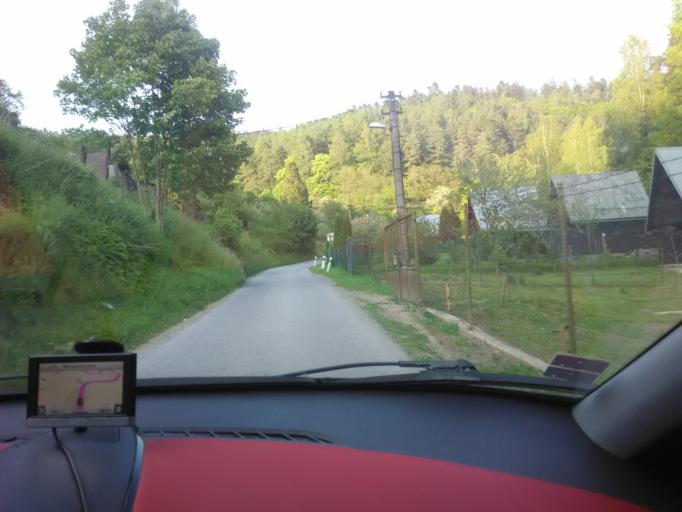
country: SK
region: Presovsky
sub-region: Okres Presov
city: Levoca
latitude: 49.0425
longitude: 20.6032
